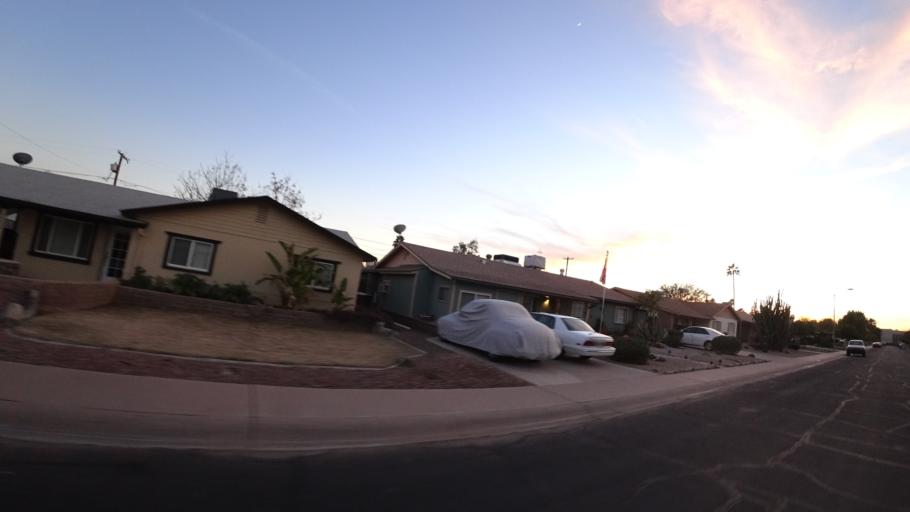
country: US
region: Arizona
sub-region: Maricopa County
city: Scottsdale
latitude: 33.4825
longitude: -111.9139
